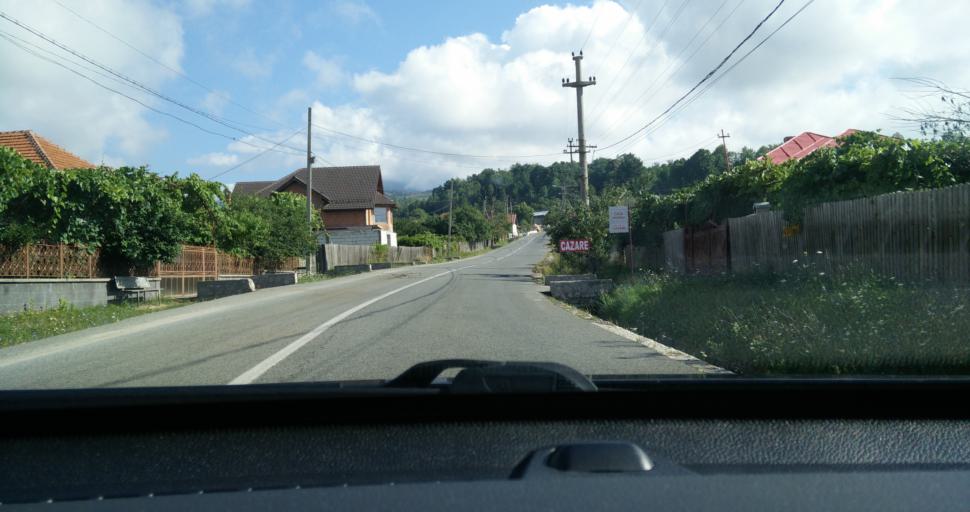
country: RO
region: Gorj
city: Novaci-Straini
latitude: 45.1805
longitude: 23.6766
